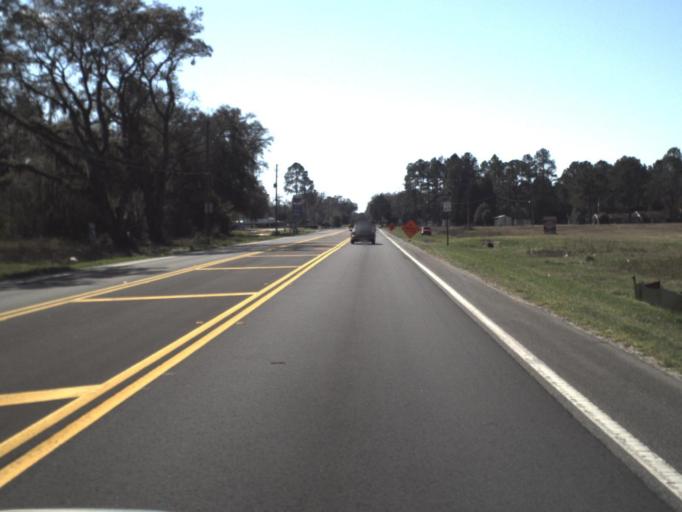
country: US
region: Florida
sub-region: Jackson County
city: Marianna
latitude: 30.7130
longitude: -85.1853
